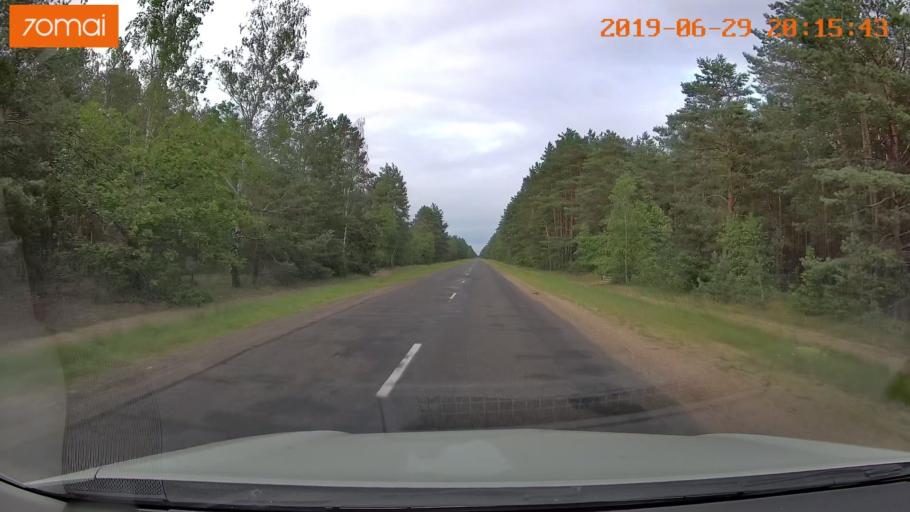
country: BY
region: Brest
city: Asnyezhytsy
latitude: 52.3762
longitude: 26.1815
